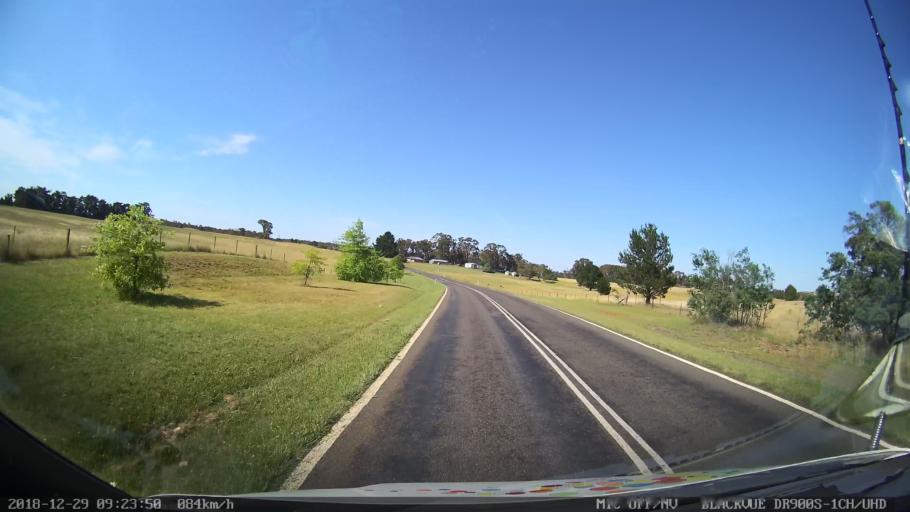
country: AU
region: New South Wales
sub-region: Upper Lachlan Shire
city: Crookwell
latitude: -34.5290
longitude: 149.3966
